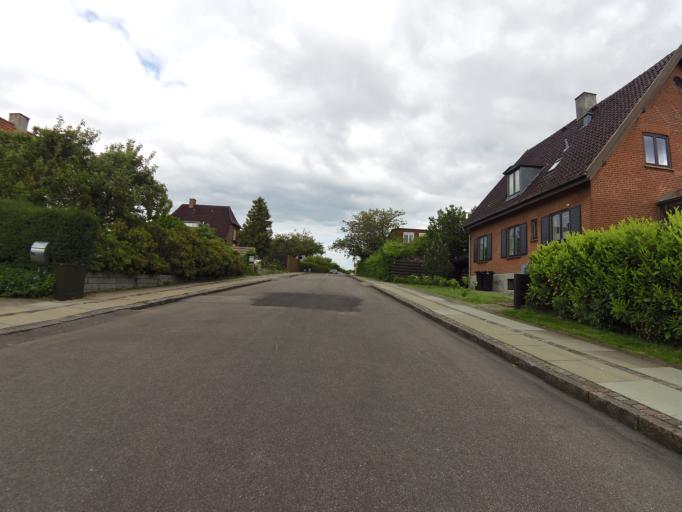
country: DK
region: Capital Region
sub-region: Frederiksberg Kommune
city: Frederiksberg
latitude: 55.7279
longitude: 12.5406
